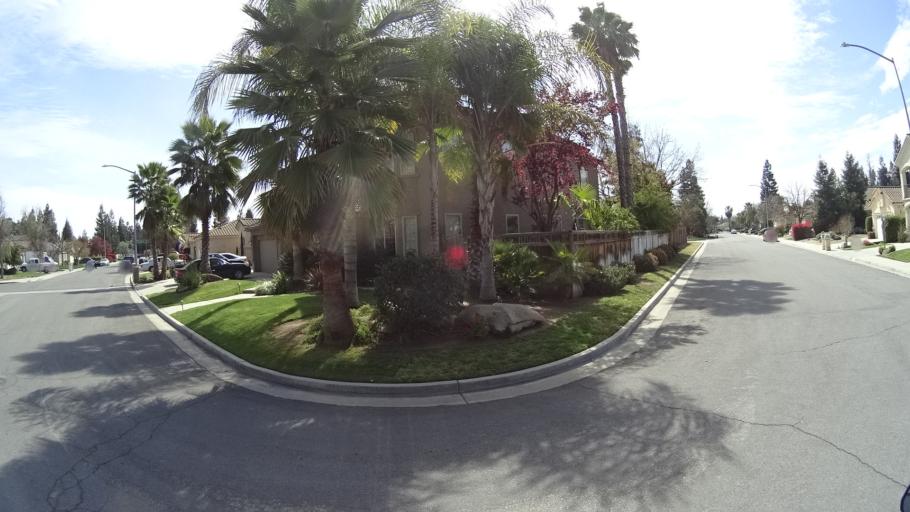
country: US
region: California
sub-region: Fresno County
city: Biola
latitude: 36.8475
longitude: -119.8921
